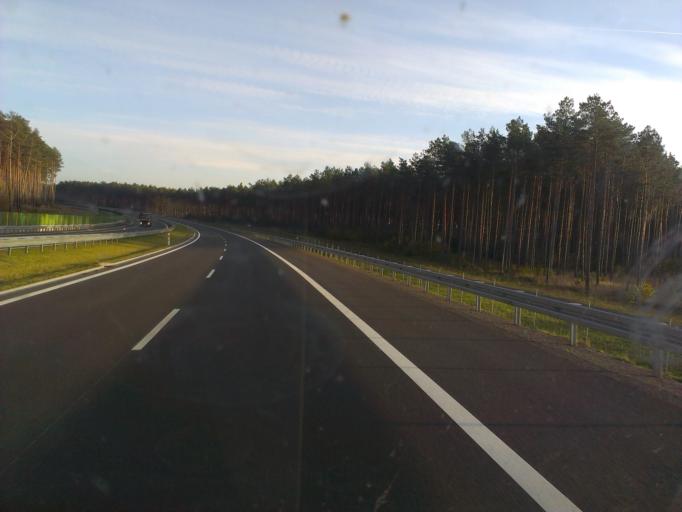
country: PL
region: Lubusz
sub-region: Powiat miedzyrzecki
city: Skwierzyna
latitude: 52.5590
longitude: 15.4773
